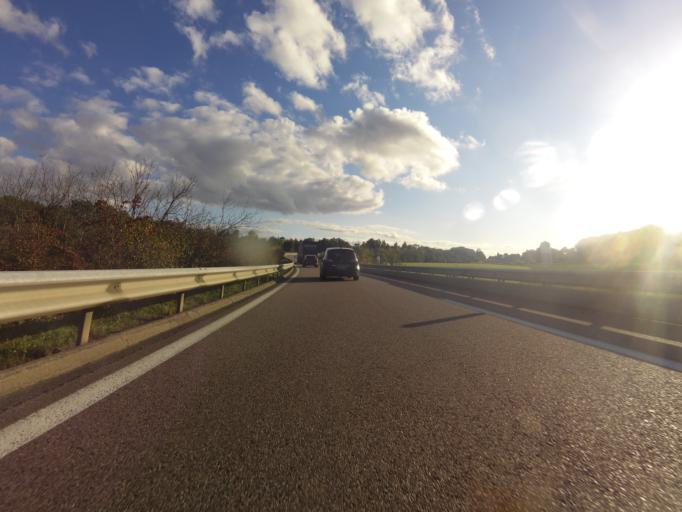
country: FR
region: Haute-Normandie
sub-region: Departement de la Seine-Maritime
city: Neufchatel-en-Bray
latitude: 49.7556
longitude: 1.4829
